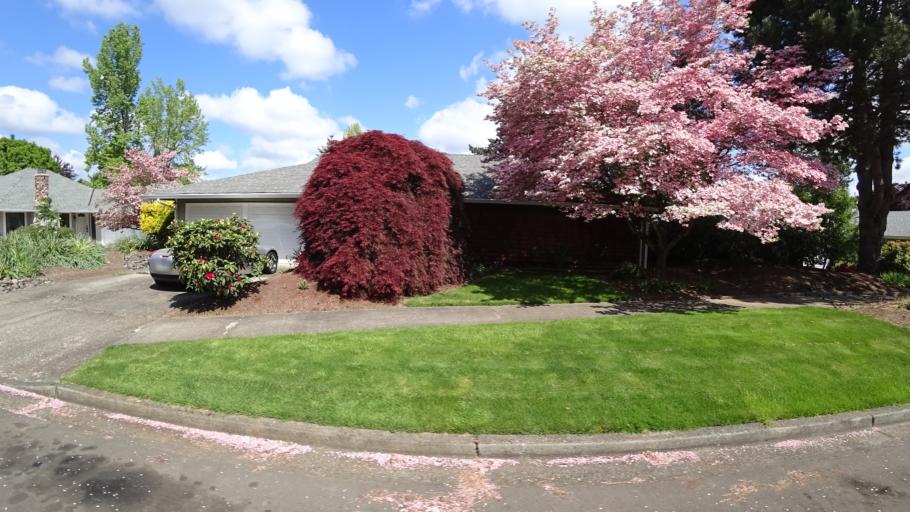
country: US
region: Oregon
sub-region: Washington County
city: Aloha
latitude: 45.5033
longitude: -122.8854
